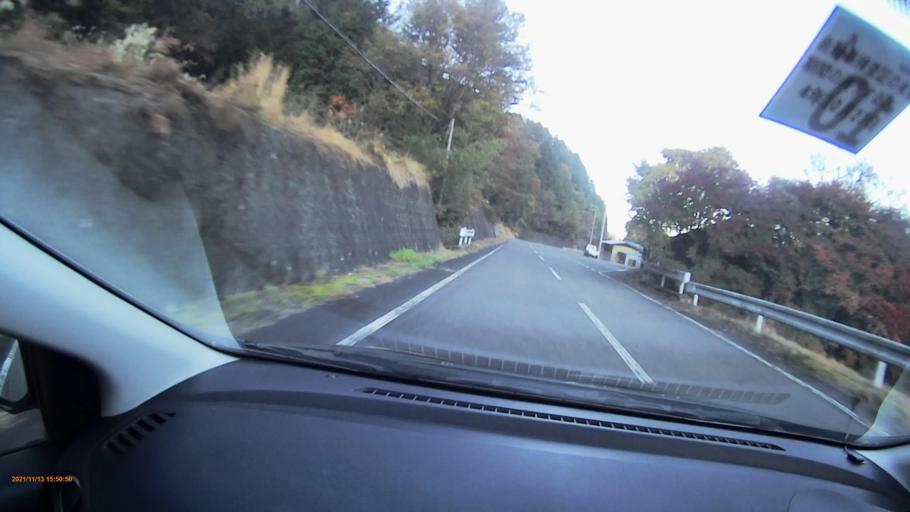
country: JP
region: Gifu
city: Nakatsugawa
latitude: 35.5969
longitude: 137.4153
